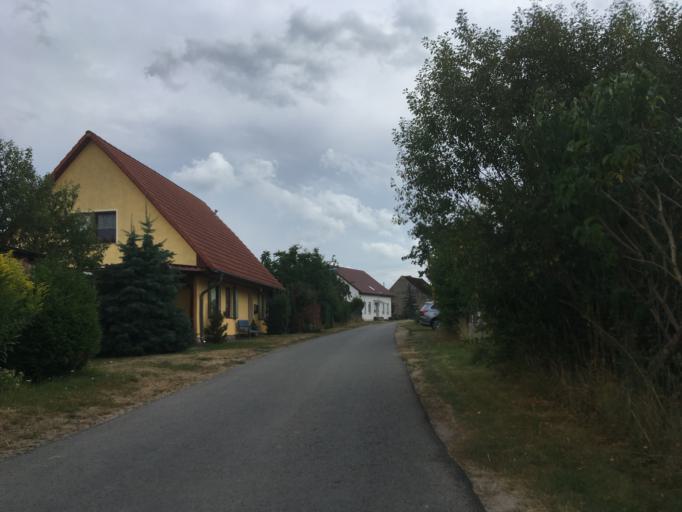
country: DE
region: Brandenburg
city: Chorin
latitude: 52.9318
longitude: 13.8609
